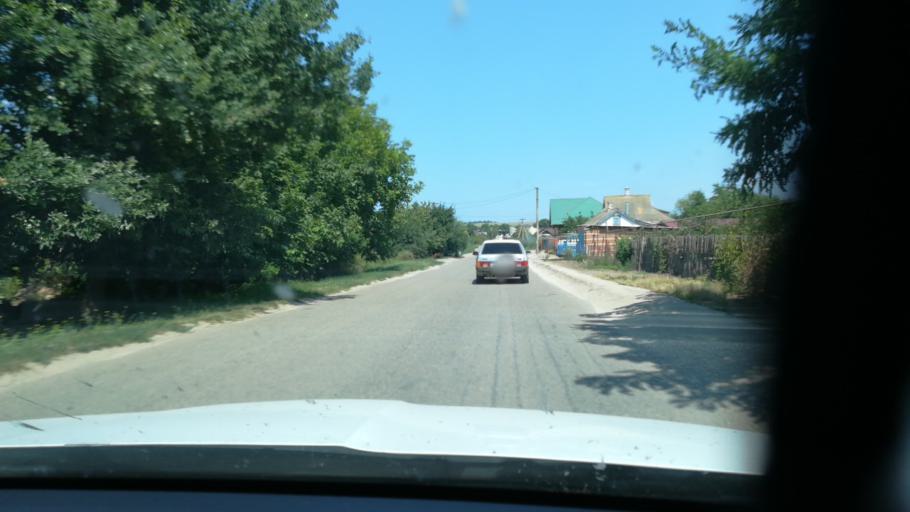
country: RU
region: Krasnodarskiy
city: Starotitarovskaya
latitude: 45.2088
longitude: 37.1457
